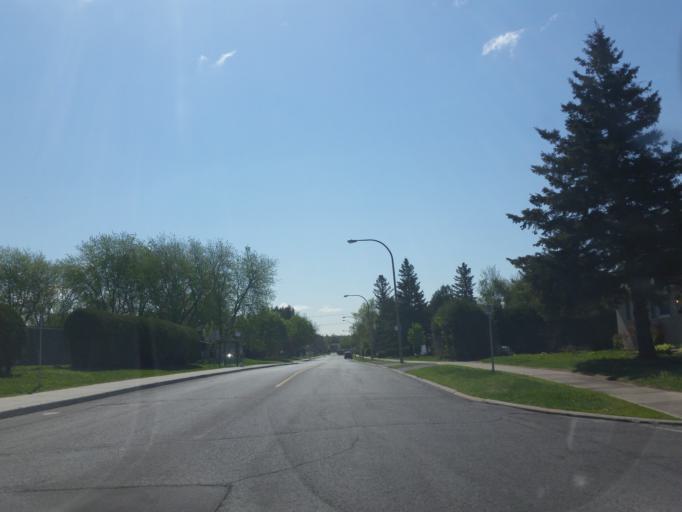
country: CA
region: Ontario
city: Ottawa
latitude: 45.3514
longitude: -75.7208
